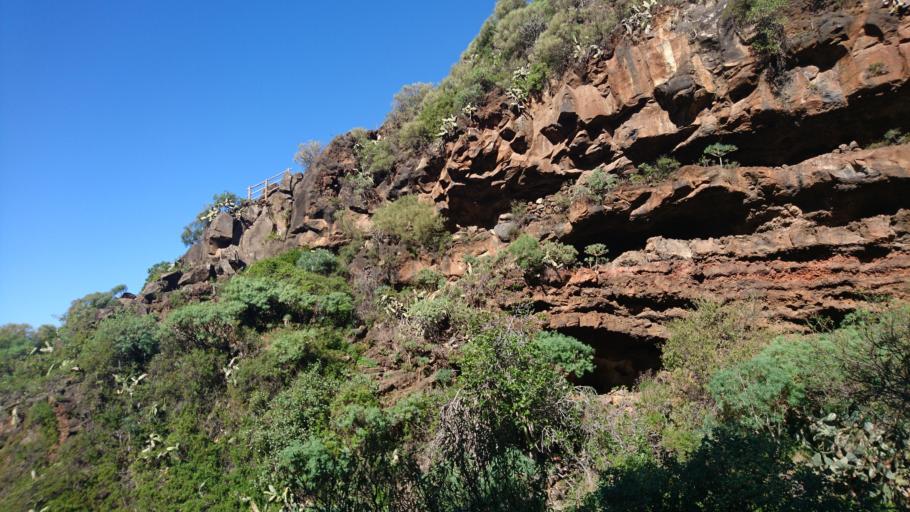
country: ES
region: Canary Islands
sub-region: Provincia de Santa Cruz de Tenerife
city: Puntagorda
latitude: 28.7928
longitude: -17.9756
